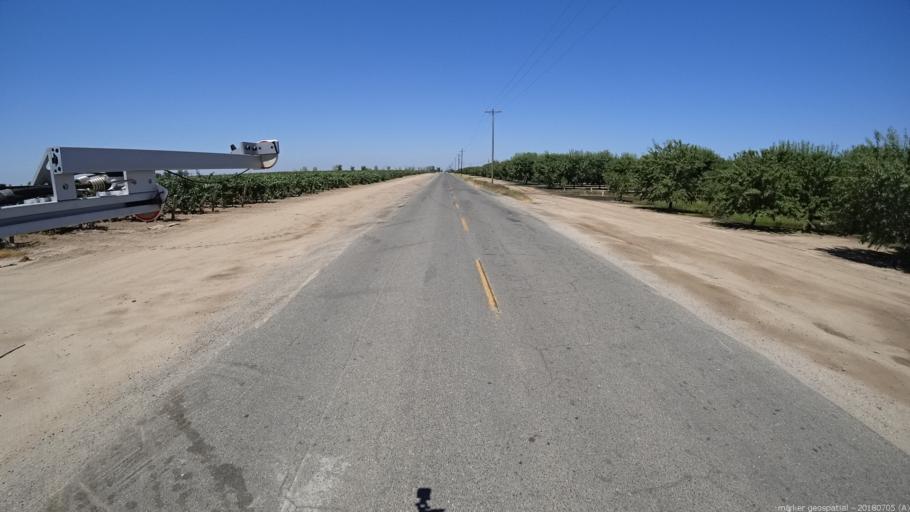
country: US
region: California
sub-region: Madera County
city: Fairmead
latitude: 37.0980
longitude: -120.1203
